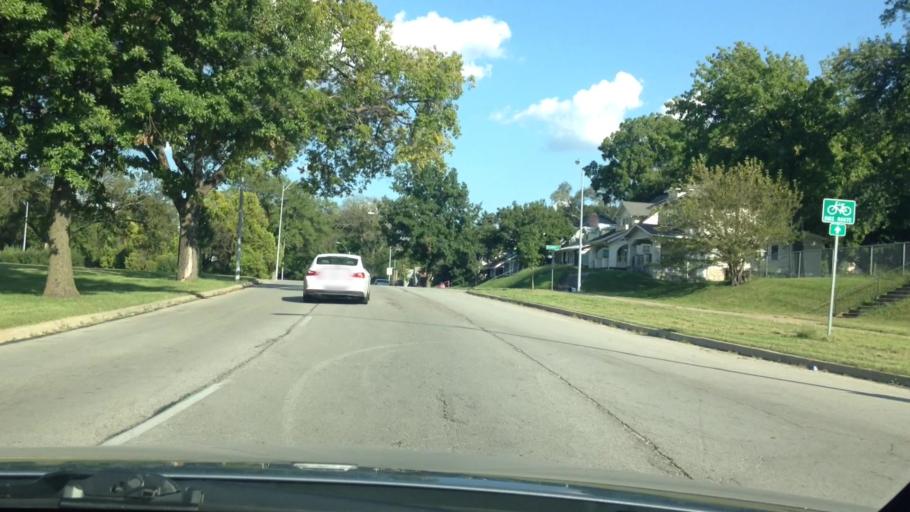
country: US
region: Kansas
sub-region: Johnson County
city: Mission Hills
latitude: 39.0069
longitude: -94.5617
